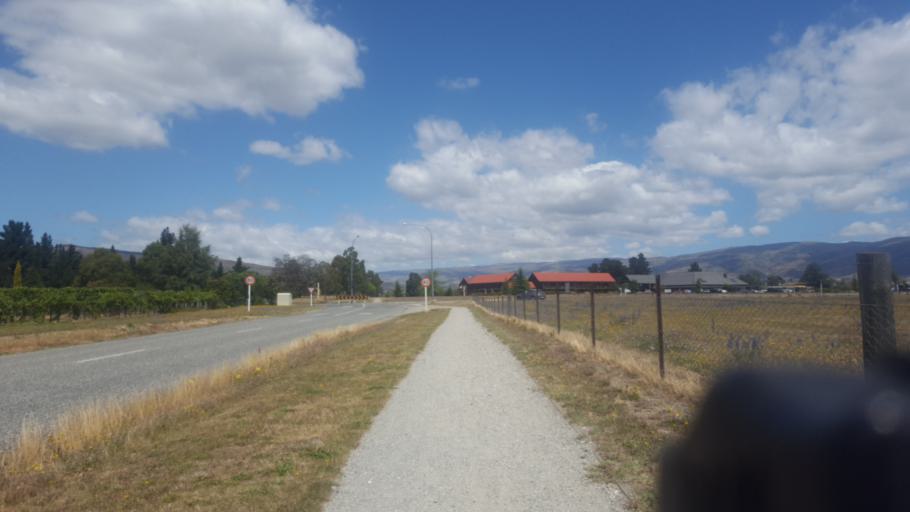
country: NZ
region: Otago
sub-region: Queenstown-Lakes District
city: Wanaka
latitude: -45.0336
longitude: 169.2024
